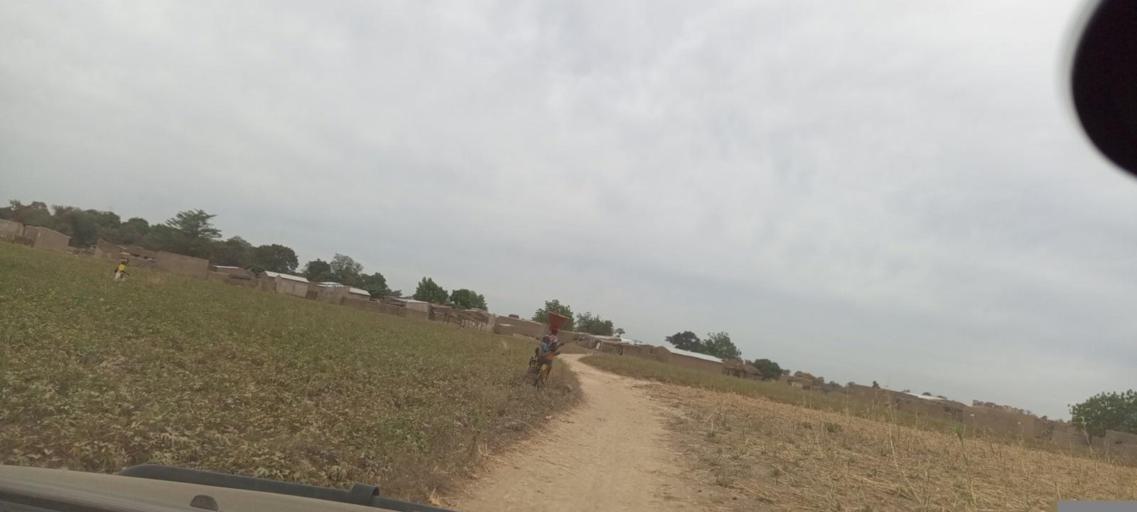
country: ML
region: Koulikoro
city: Kati
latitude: 12.7476
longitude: -8.3589
